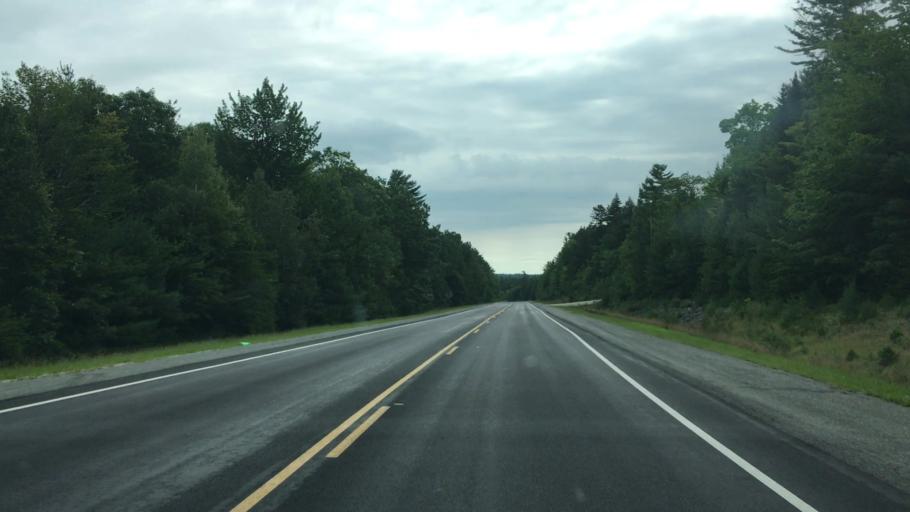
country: US
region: Maine
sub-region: Washington County
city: Addison
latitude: 44.9106
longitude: -67.8509
